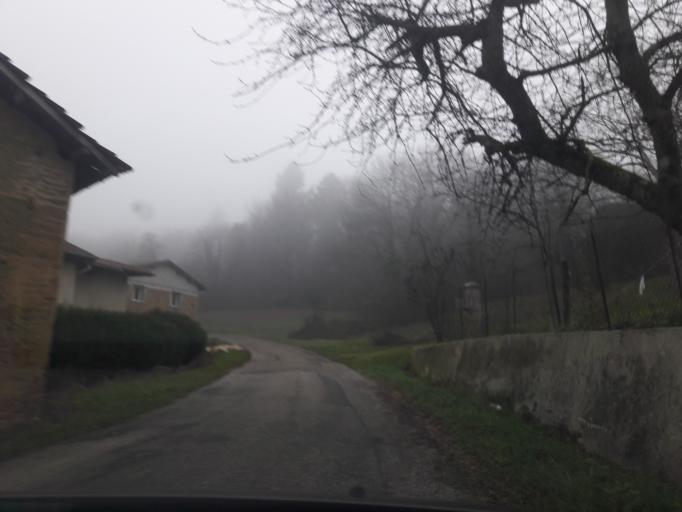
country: FR
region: Rhone-Alpes
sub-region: Departement de l'Isere
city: Saint-Jean-de-Bournay
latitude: 45.4186
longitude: 5.1490
